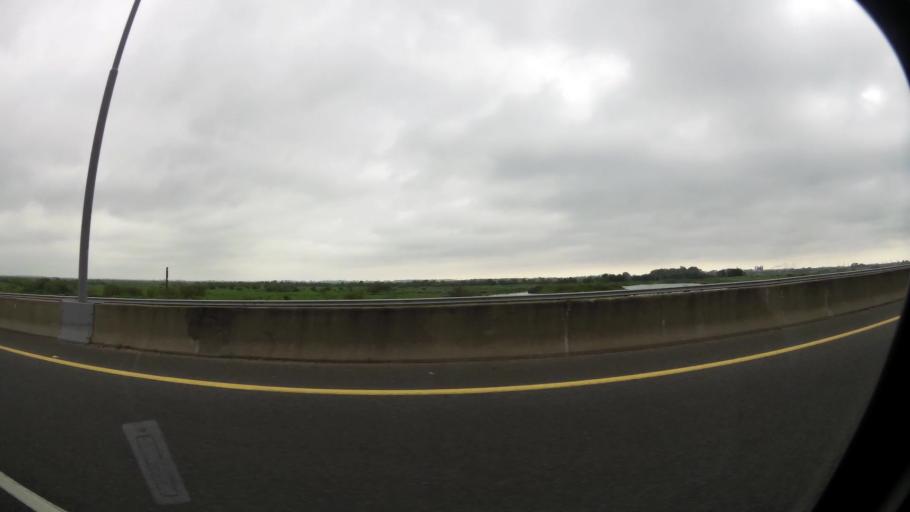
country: AR
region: Buenos Aires
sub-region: Partido de La Plata
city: La Plata
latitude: -34.8730
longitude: -57.9782
